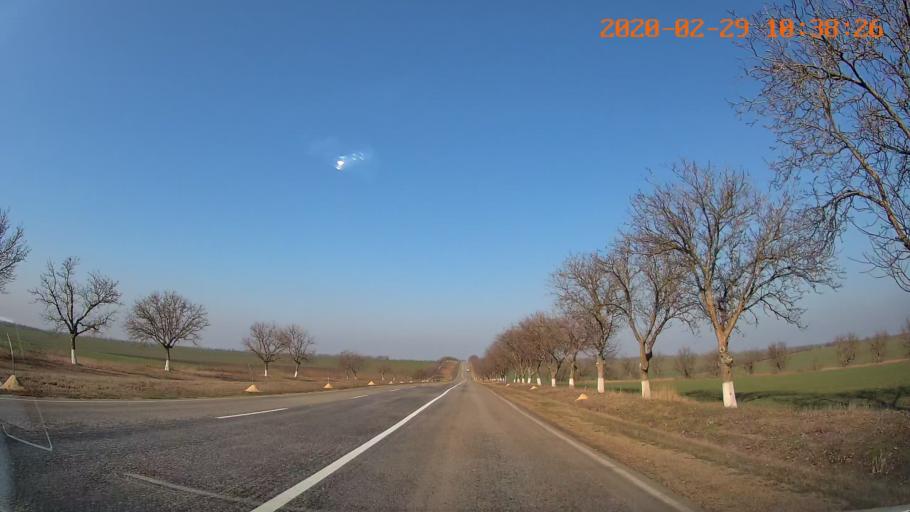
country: MD
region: Anenii Noi
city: Varnita
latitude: 47.0160
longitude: 29.4733
